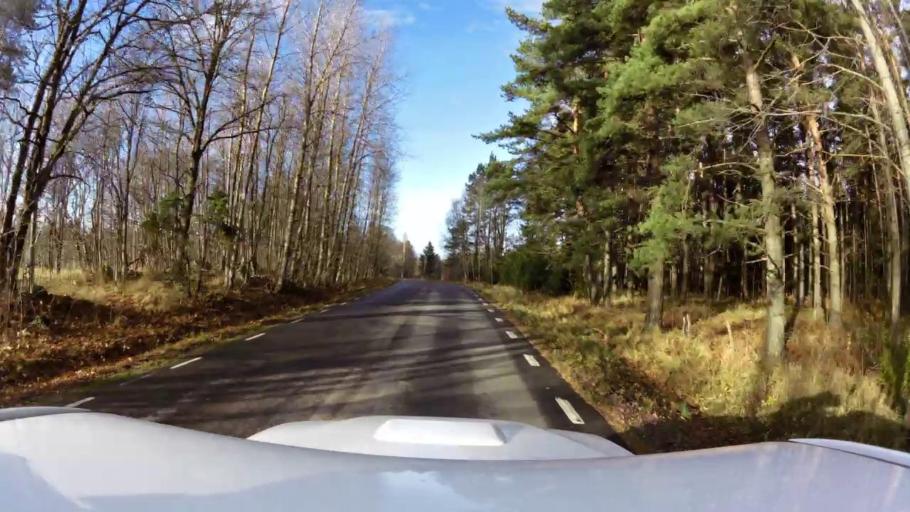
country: SE
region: OEstergoetland
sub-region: Linkopings Kommun
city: Sturefors
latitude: 58.3210
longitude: 15.6514
